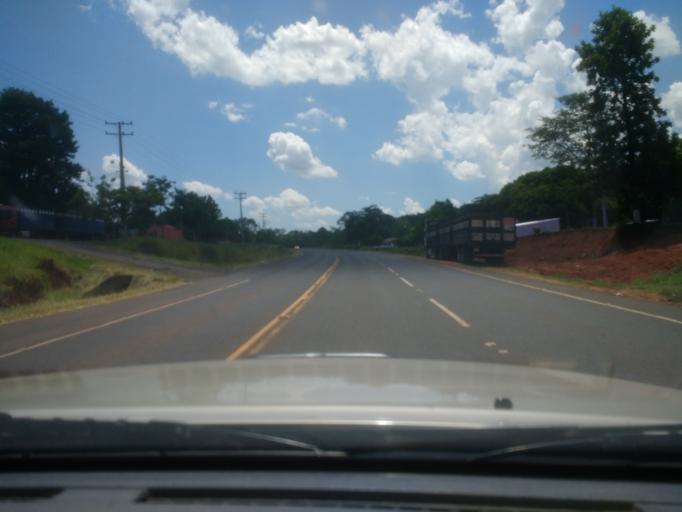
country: PY
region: San Pedro
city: Guayaybi
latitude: -24.5954
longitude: -56.5089
